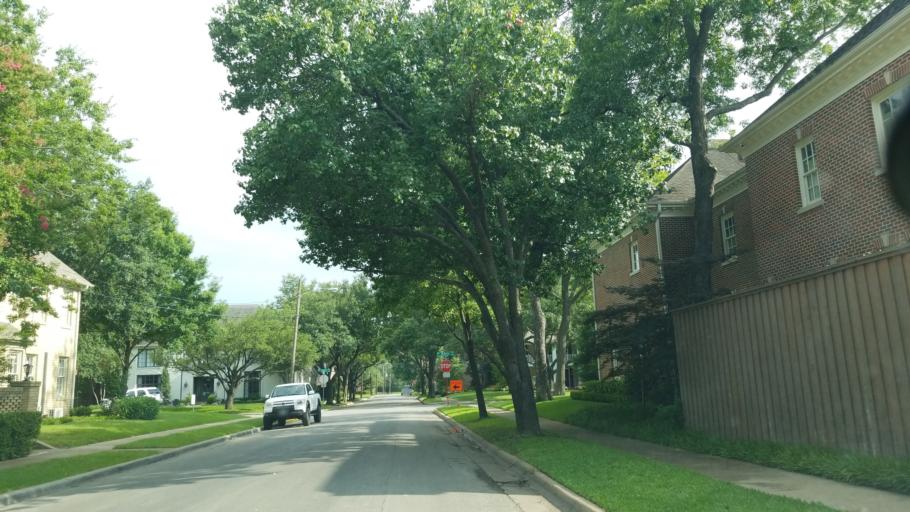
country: US
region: Texas
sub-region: Dallas County
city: University Park
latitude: 32.8446
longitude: -96.8021
